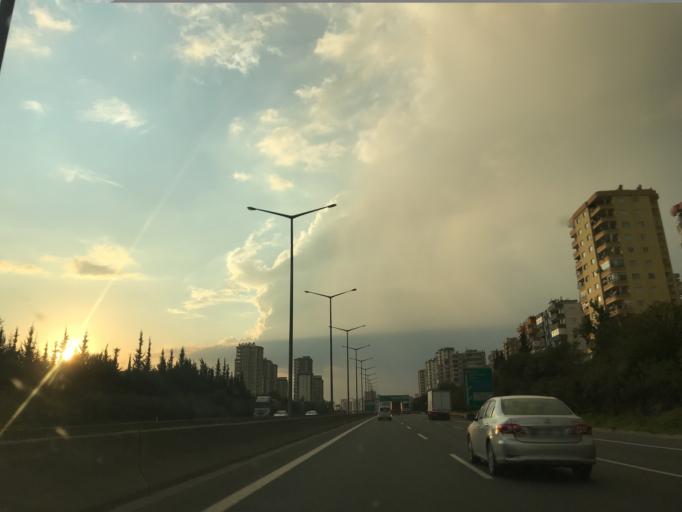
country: TR
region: Adana
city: Seyhan
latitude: 37.0311
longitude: 35.2654
